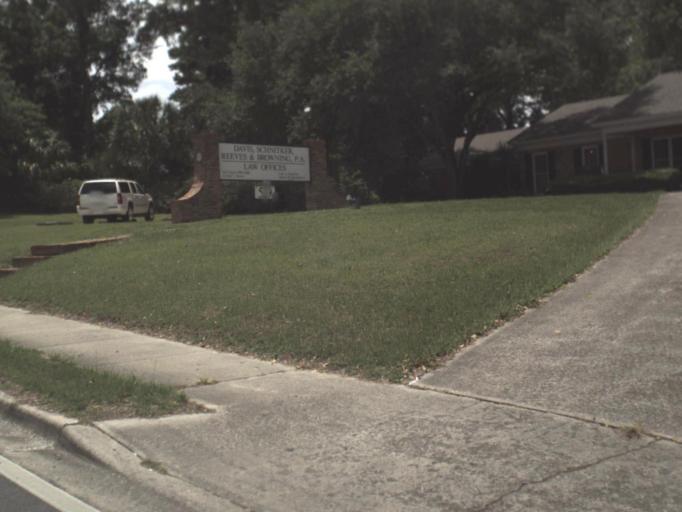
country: US
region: Florida
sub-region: Madison County
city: Madison
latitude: 30.4702
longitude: -83.4220
